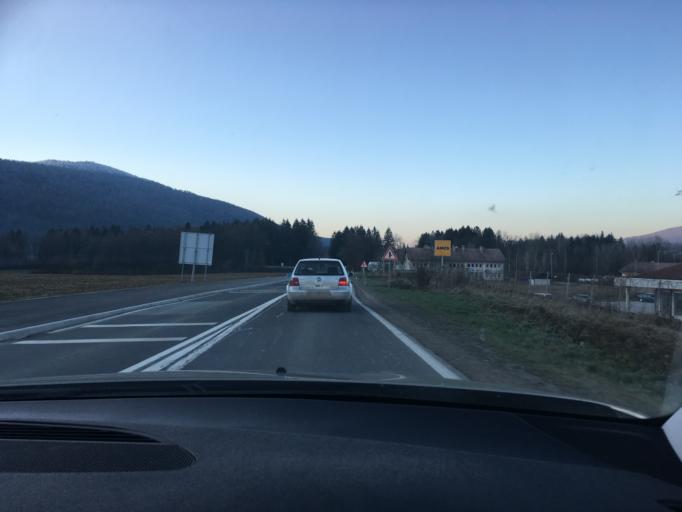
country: SI
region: Kocevje
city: Kocevje
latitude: 45.6533
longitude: 14.8509
